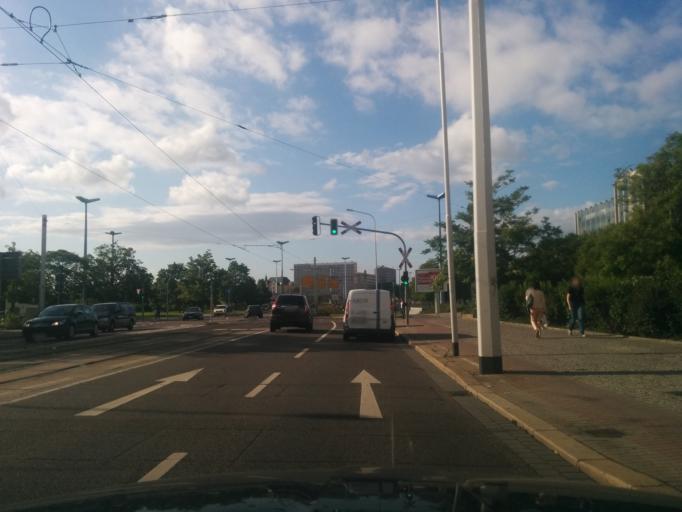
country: DE
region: Saxony-Anhalt
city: Halle (Saale)
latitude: 51.4813
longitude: 11.9820
